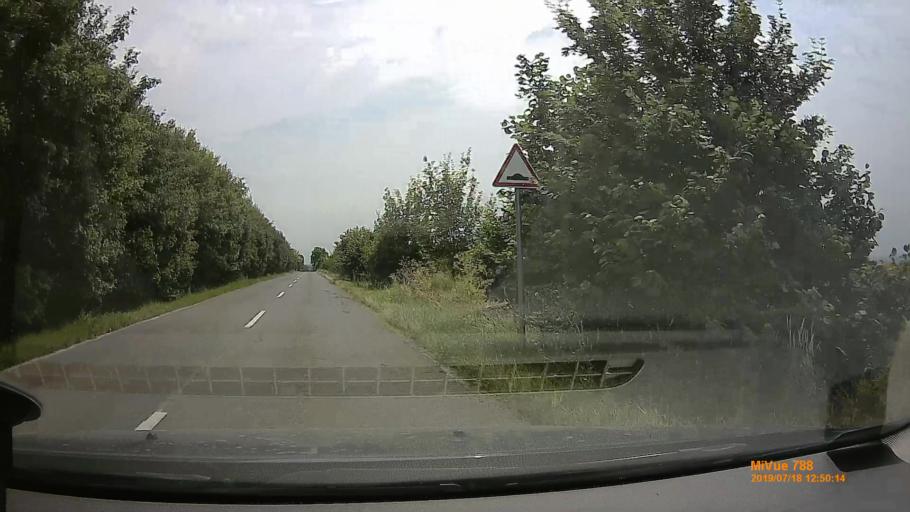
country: HU
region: Pest
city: Perbal
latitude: 47.5699
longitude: 18.7884
